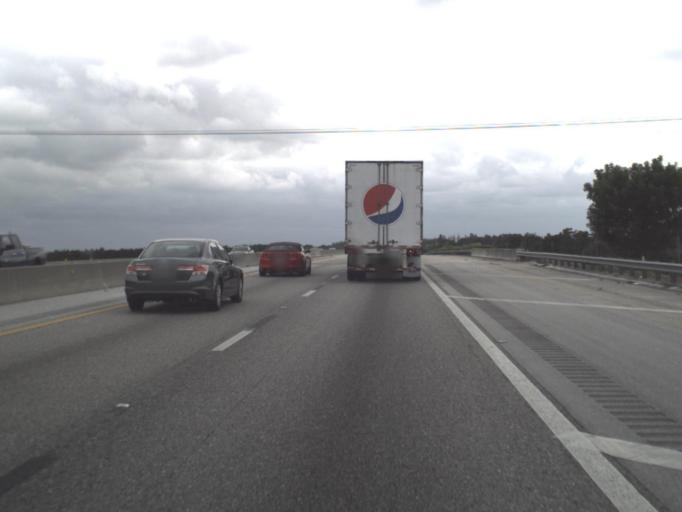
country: US
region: Florida
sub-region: Palm Beach County
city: Greenacres City
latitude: 26.5913
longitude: -80.1735
